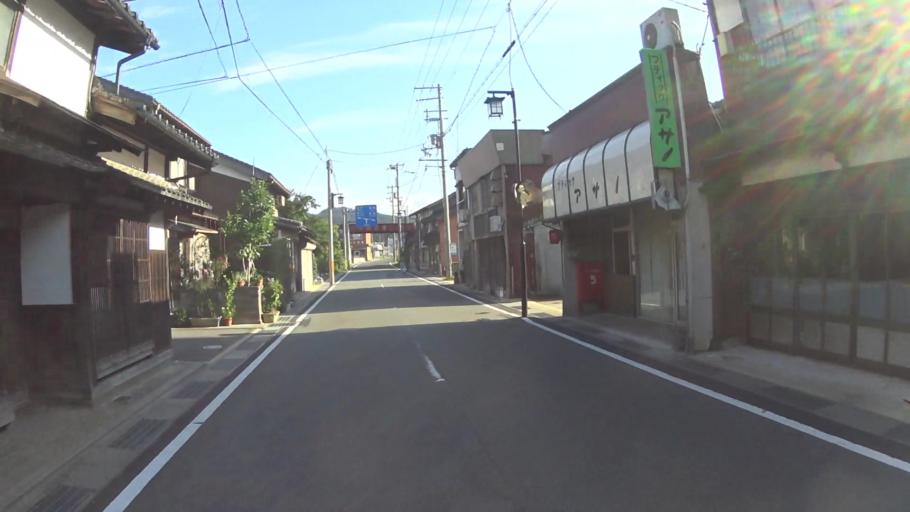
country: JP
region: Hyogo
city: Toyooka
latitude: 35.6044
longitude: 134.9009
